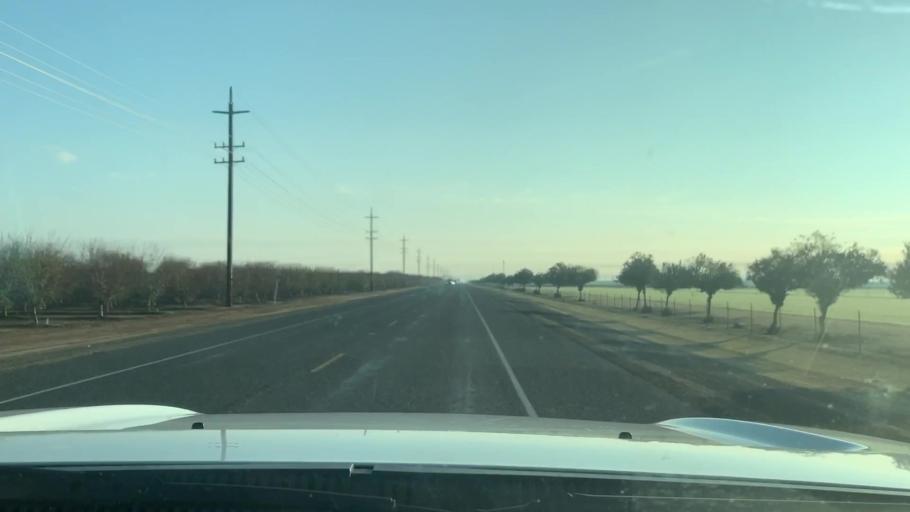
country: US
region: California
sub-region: Kern County
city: Wasco
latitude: 35.6014
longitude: -119.4152
